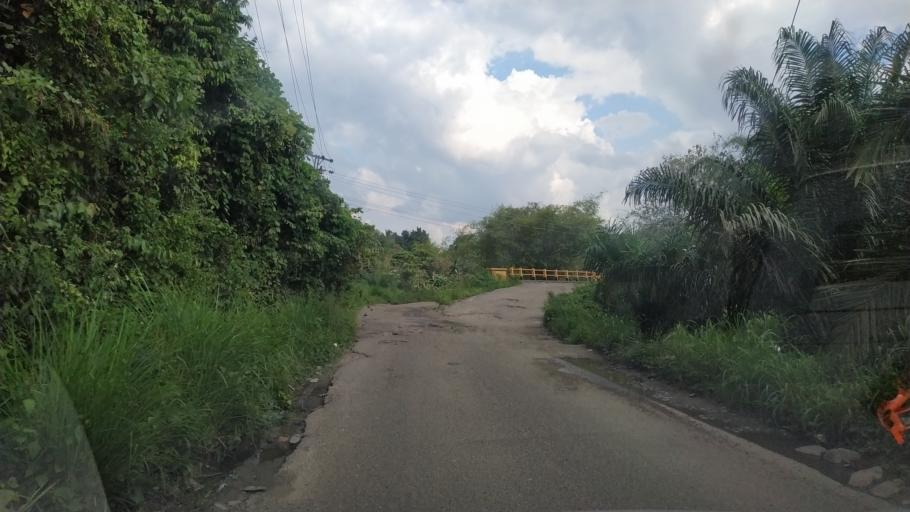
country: ID
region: North Sumatra
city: Binanga
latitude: 1.2485
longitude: 99.7494
